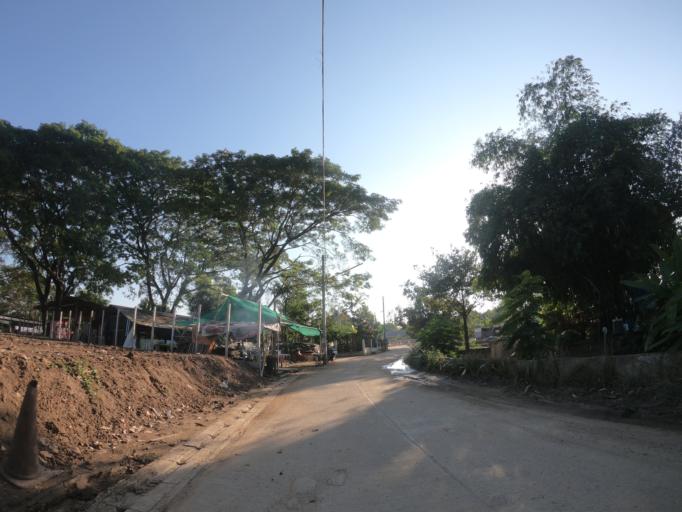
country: TH
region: Chiang Mai
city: Chiang Mai
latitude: 18.7423
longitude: 98.9810
